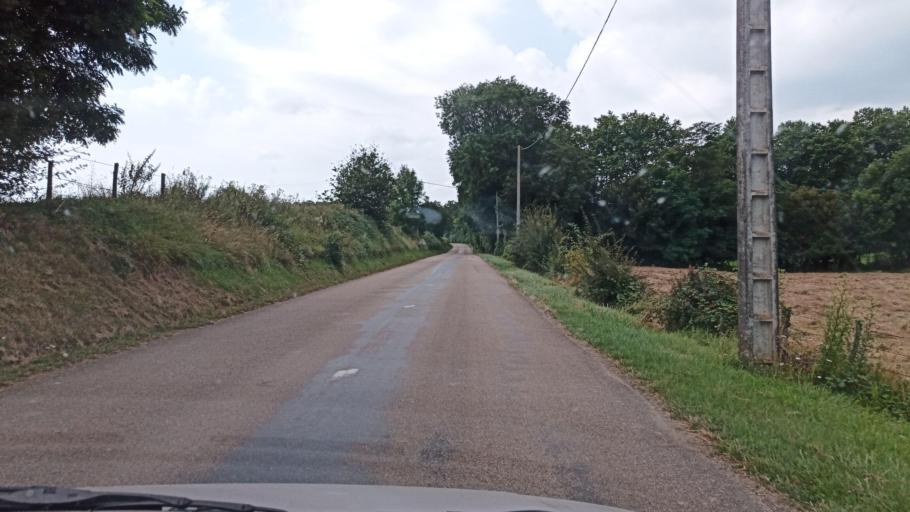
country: FR
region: Bourgogne
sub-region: Departement de l'Yonne
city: Egriselles-le-Bocage
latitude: 48.0217
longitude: 3.1728
